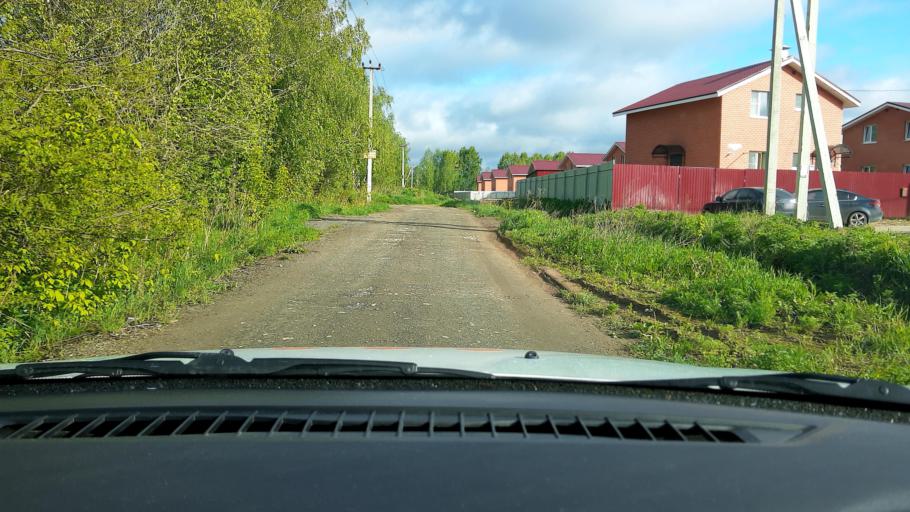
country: RU
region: Nizjnij Novgorod
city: Afonino
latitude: 56.1950
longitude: 44.0688
